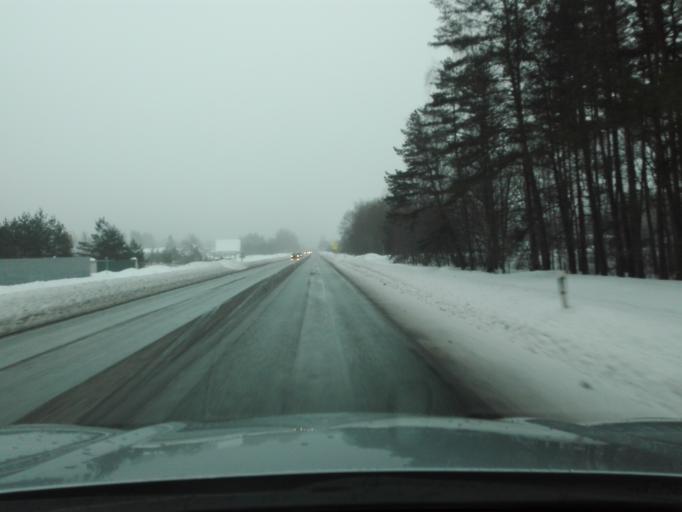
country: EE
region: Harju
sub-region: Kiili vald
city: Kiili
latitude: 59.3437
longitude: 24.7740
